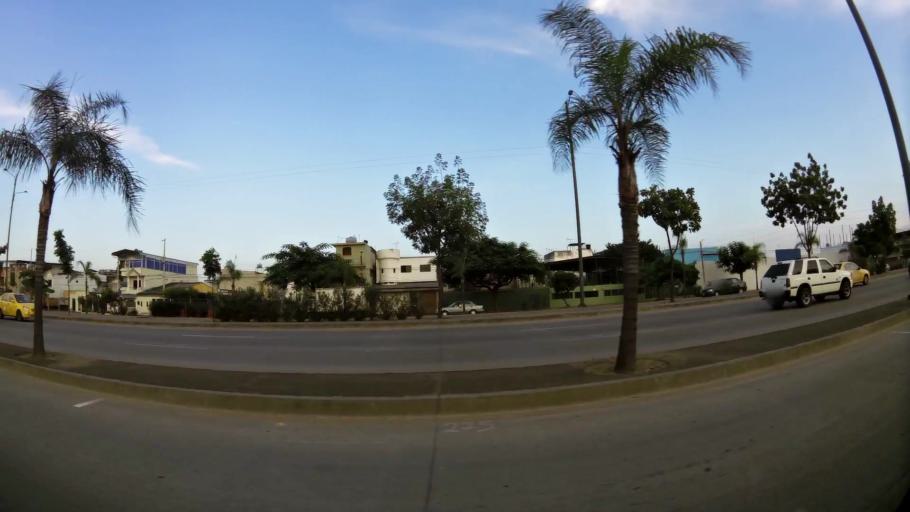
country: EC
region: Guayas
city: Eloy Alfaro
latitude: -2.1195
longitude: -79.8828
